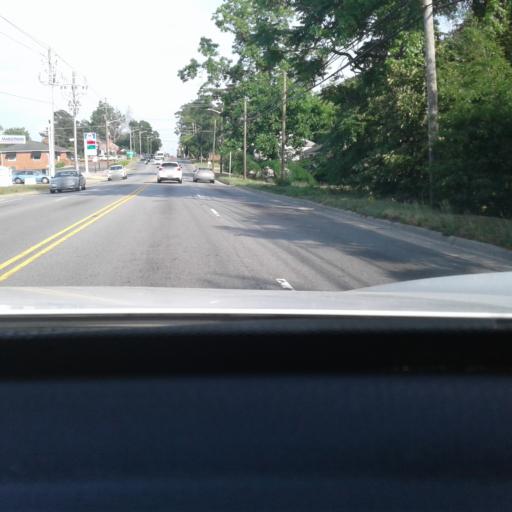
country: US
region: North Carolina
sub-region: Harnett County
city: Dunn
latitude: 35.3121
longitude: -78.6192
